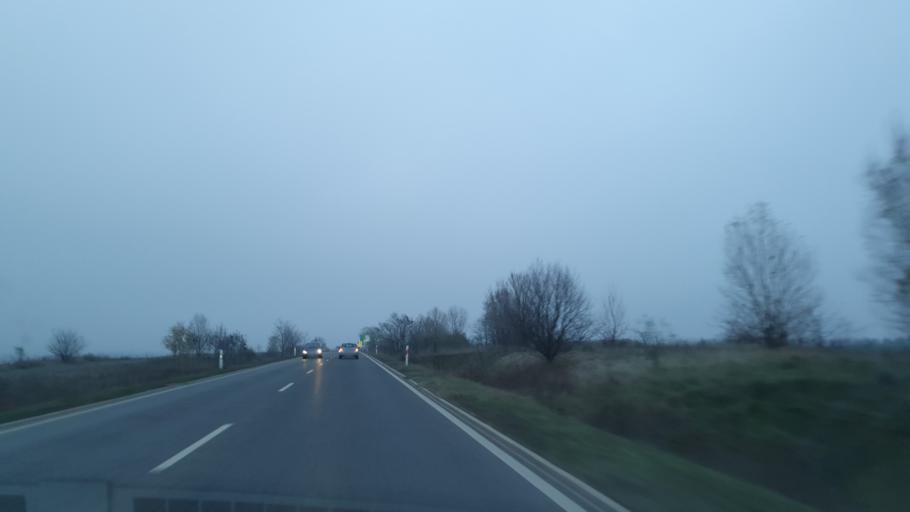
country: HU
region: Pest
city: Csomor
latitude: 47.5493
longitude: 19.1957
